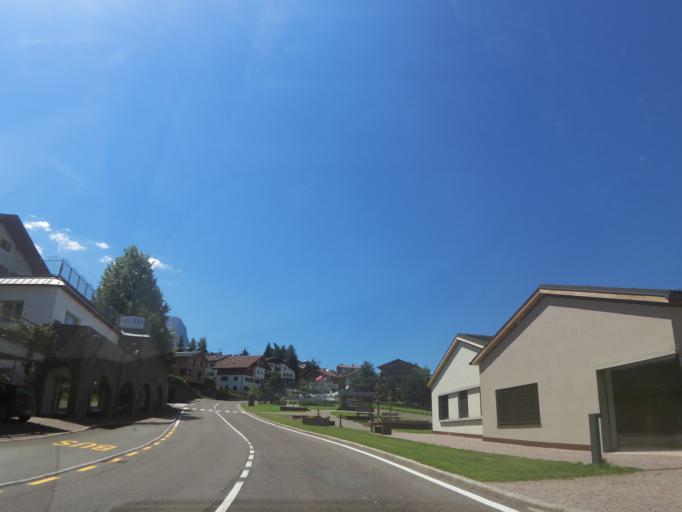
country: IT
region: Trentino-Alto Adige
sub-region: Bolzano
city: Castelrotto
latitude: 46.5662
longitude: 11.5592
